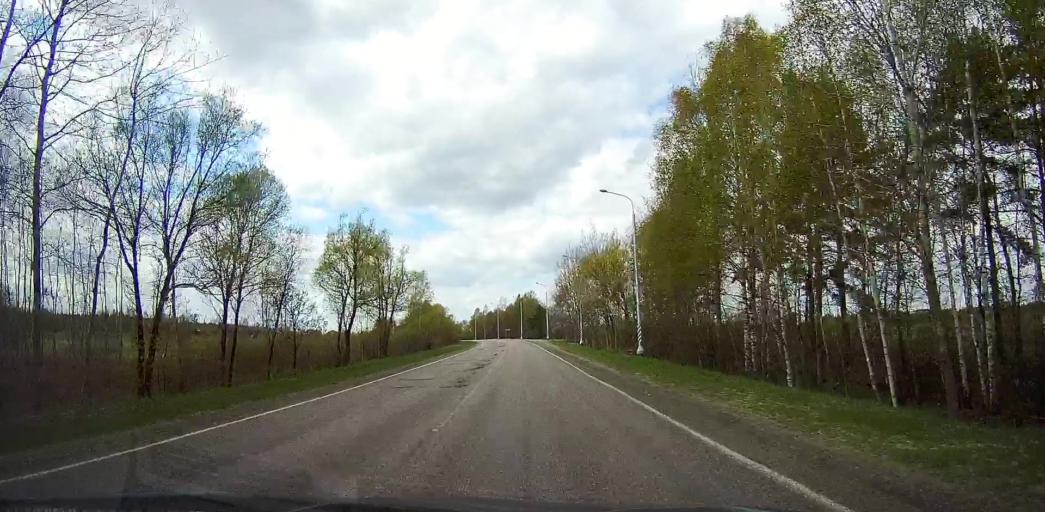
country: RU
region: Moskovskaya
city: Davydovo
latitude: 55.6629
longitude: 38.8058
